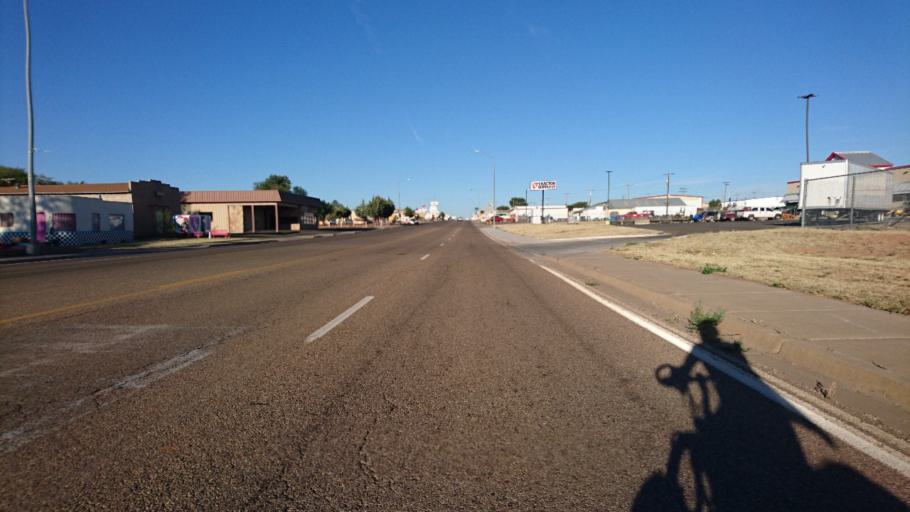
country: US
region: New Mexico
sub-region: Quay County
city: Tucumcari
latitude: 35.1719
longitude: -103.7084
